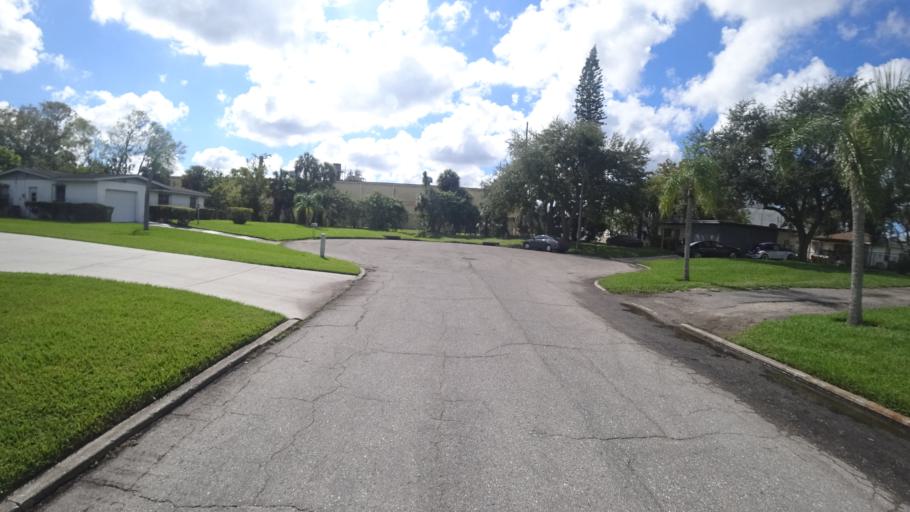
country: US
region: Florida
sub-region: Manatee County
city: Samoset
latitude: 27.4847
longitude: -82.5484
